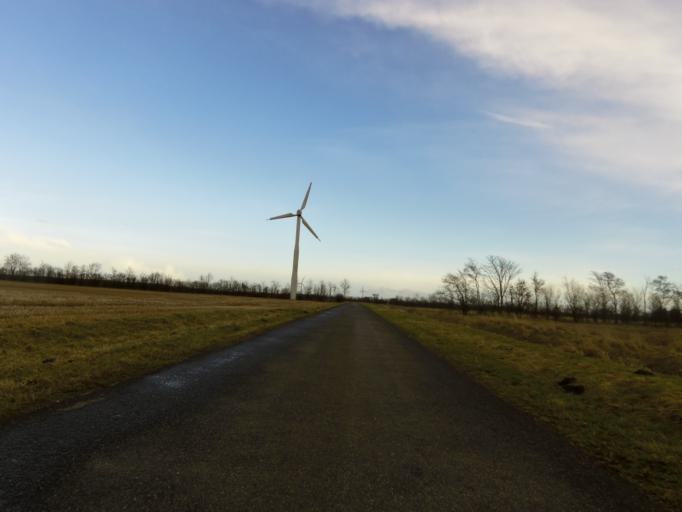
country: DK
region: South Denmark
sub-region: Haderslev Kommune
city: Gram
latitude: 55.2399
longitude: 9.0549
